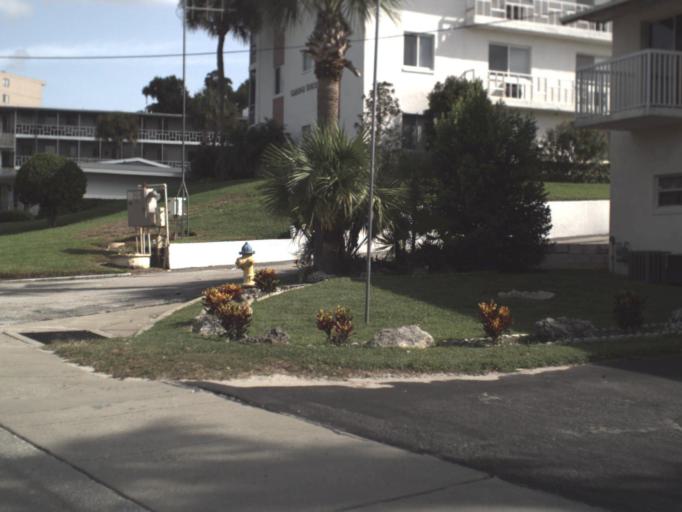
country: US
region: Florida
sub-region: Polk County
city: Winter Haven
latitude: 28.0388
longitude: -81.7333
